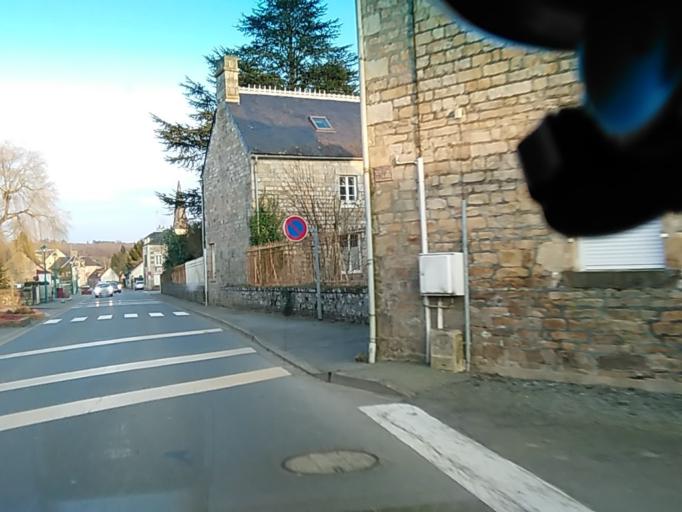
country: FR
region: Lower Normandy
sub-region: Departement de l'Orne
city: Tesse-la-Madeleine
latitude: 48.5802
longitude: -0.4188
